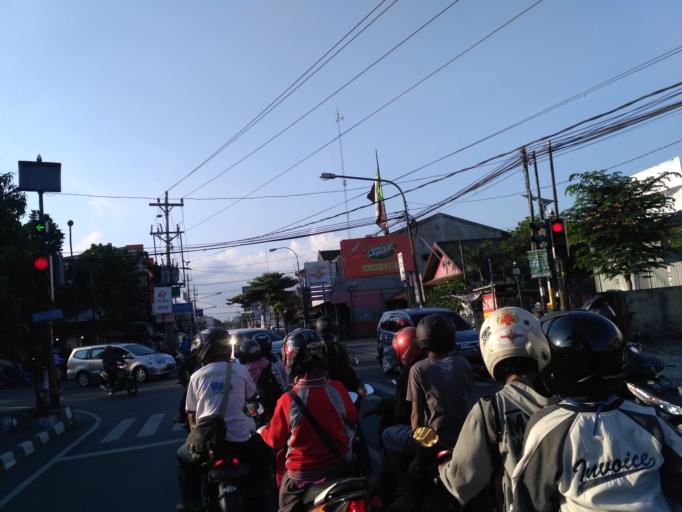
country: ID
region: Daerah Istimewa Yogyakarta
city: Yogyakarta
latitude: -7.8262
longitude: 110.3901
